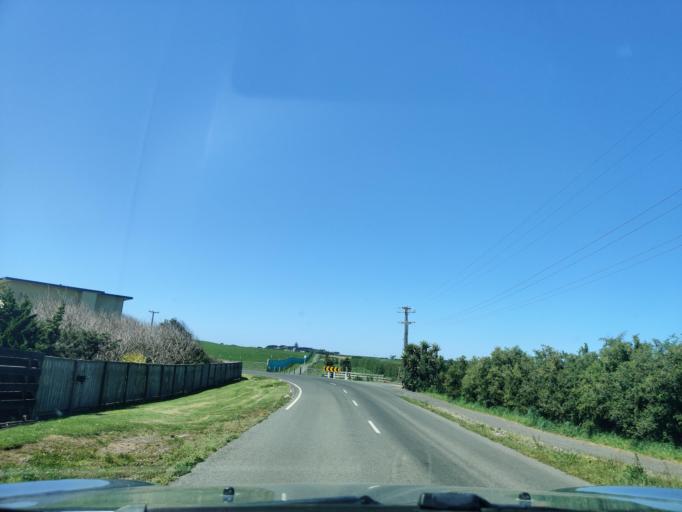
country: NZ
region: Taranaki
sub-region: South Taranaki District
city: Hawera
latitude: -39.6022
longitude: 174.2594
